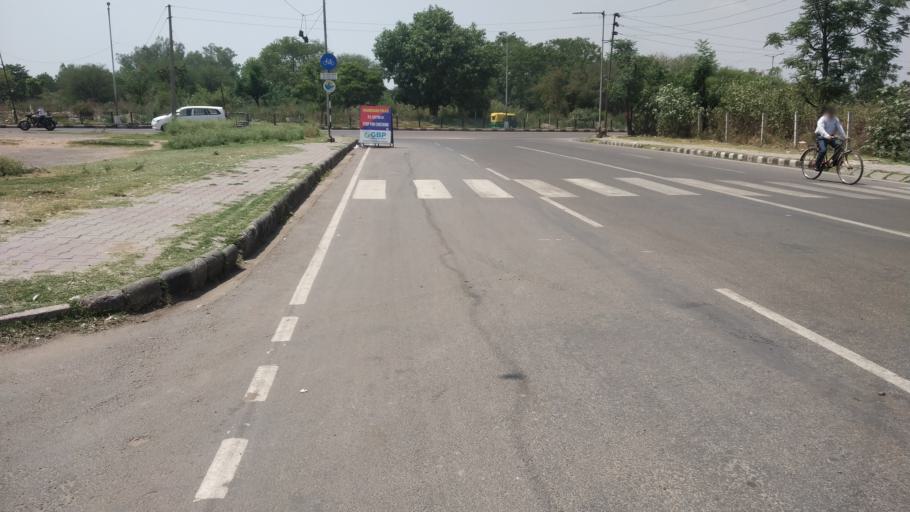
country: IN
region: Punjab
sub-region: Ajitgarh
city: Mohali
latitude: 30.7138
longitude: 76.7326
